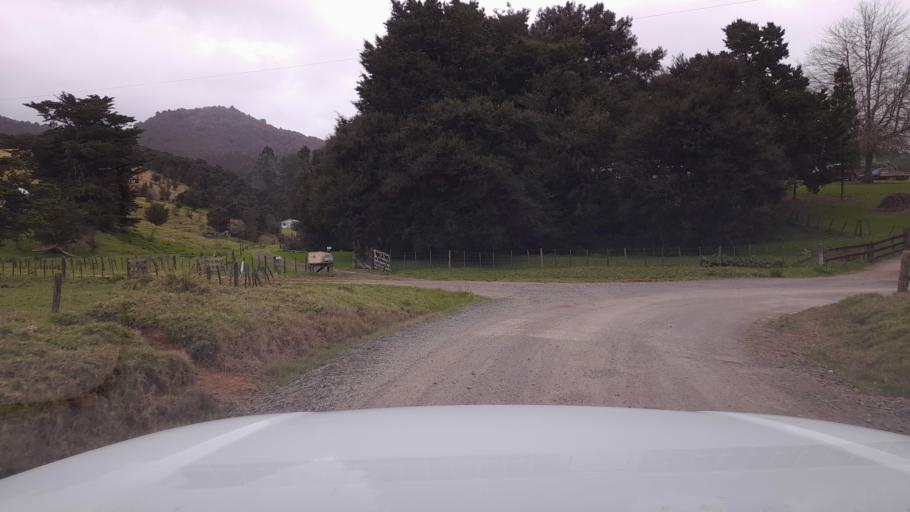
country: NZ
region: Northland
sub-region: Far North District
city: Paihia
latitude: -35.3388
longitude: 174.2345
